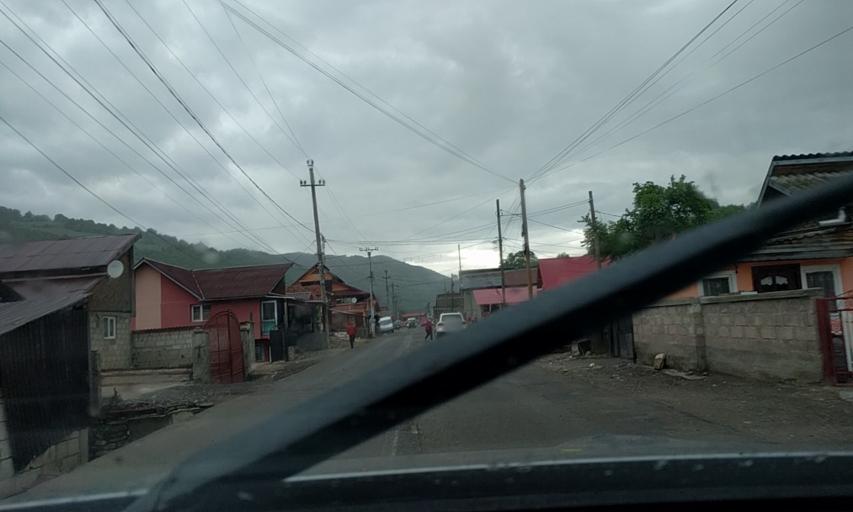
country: RO
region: Dambovita
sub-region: Comuna Moroeni
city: Glod
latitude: 45.2378
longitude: 25.4464
